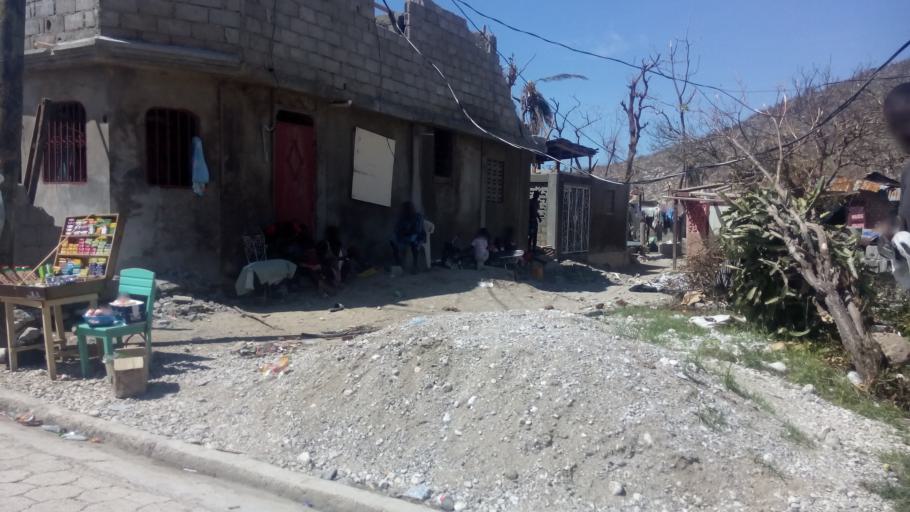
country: HT
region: Sud
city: Port-a-Piment
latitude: 18.2599
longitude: -74.0997
